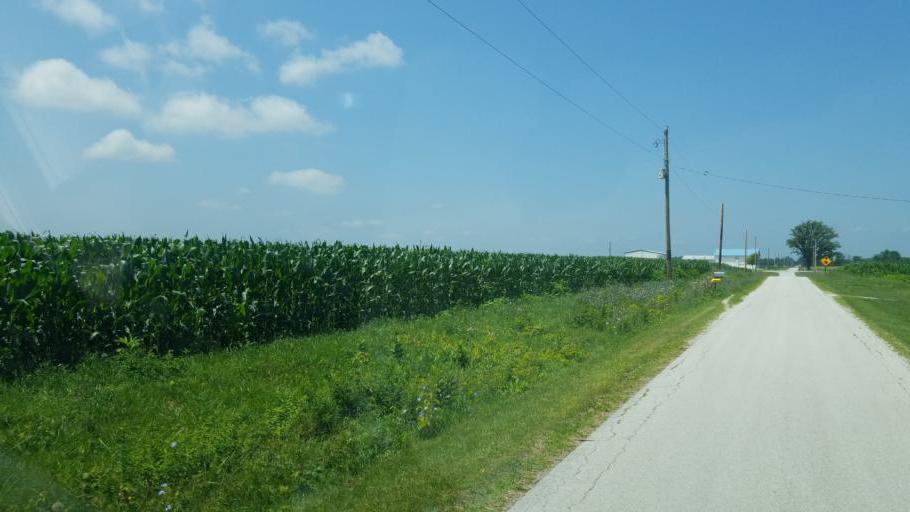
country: US
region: Ohio
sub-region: Sandusky County
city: Green Springs
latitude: 41.1980
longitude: -82.9921
